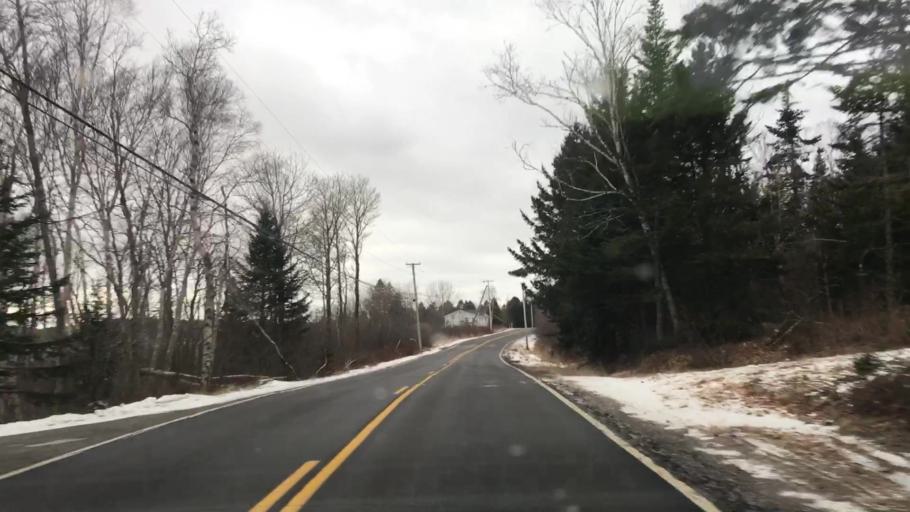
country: US
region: Maine
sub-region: Washington County
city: Machiasport
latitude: 44.7020
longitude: -67.3406
